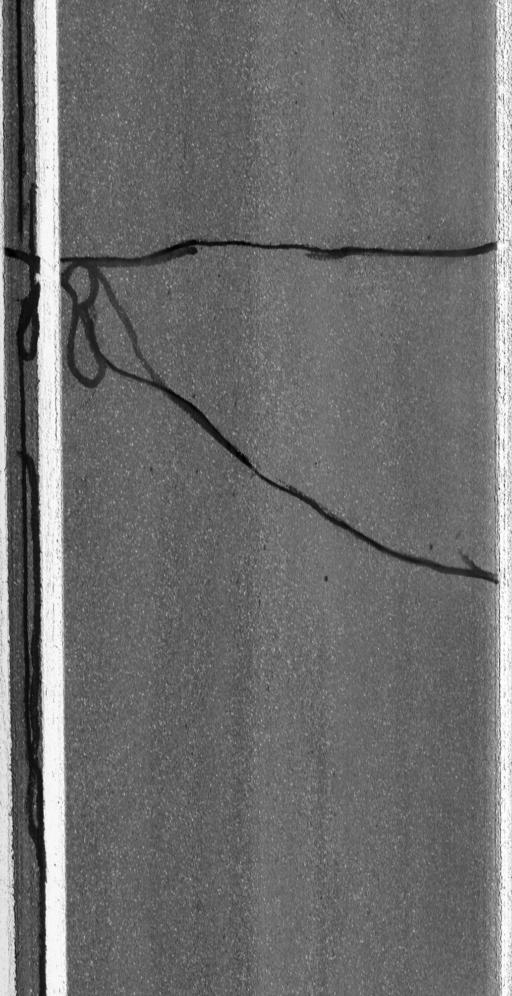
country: US
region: Vermont
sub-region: Orleans County
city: Newport
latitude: 45.0041
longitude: -72.0880
